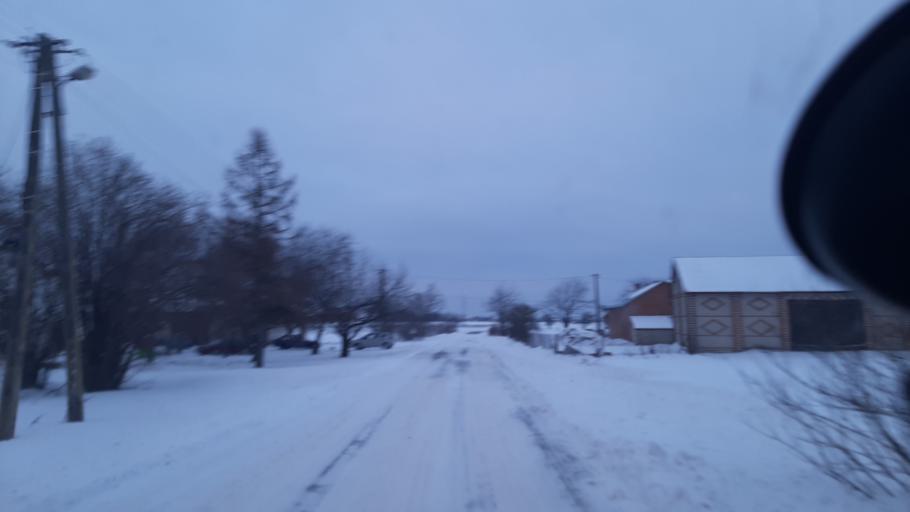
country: PL
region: Lublin Voivodeship
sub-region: Powiat lubelski
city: Jastkow
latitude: 51.3457
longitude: 22.4096
